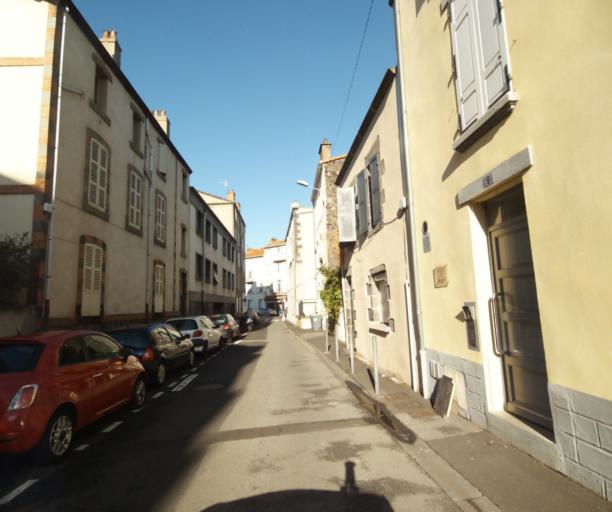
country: FR
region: Auvergne
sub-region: Departement du Puy-de-Dome
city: Clermont-Ferrand
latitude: 45.7729
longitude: 3.0935
